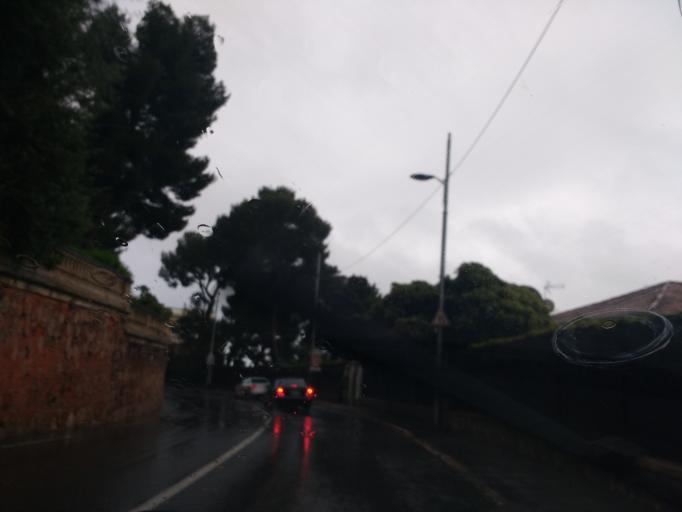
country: FR
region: Provence-Alpes-Cote d'Azur
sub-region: Departement des Alpes-Maritimes
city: Cap-d'Ail
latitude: 43.7229
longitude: 7.3935
